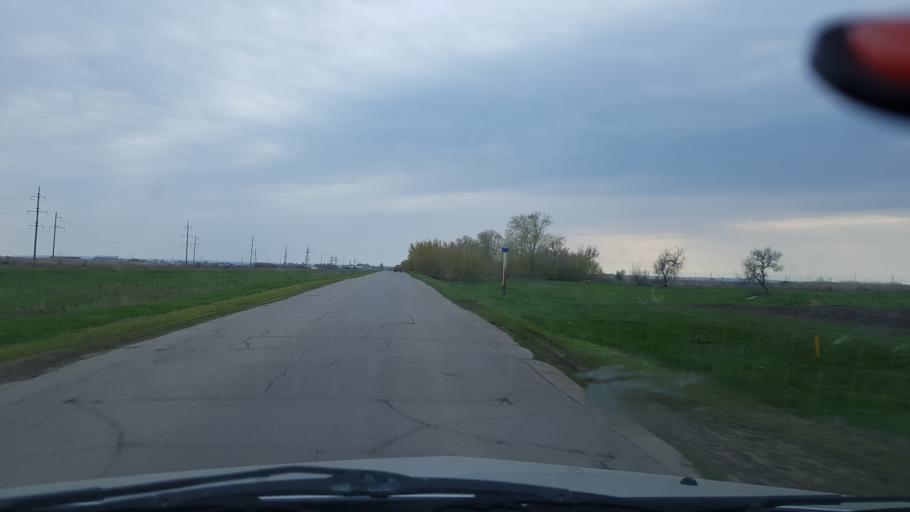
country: RU
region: Samara
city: Khryashchevka
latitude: 53.6707
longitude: 49.1072
